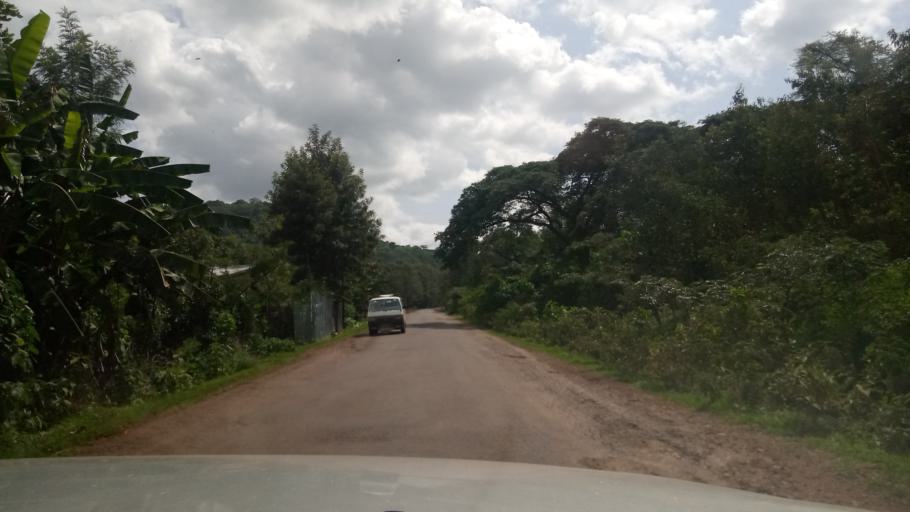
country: ET
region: Oromiya
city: Agaro
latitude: 7.9210
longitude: 36.5253
